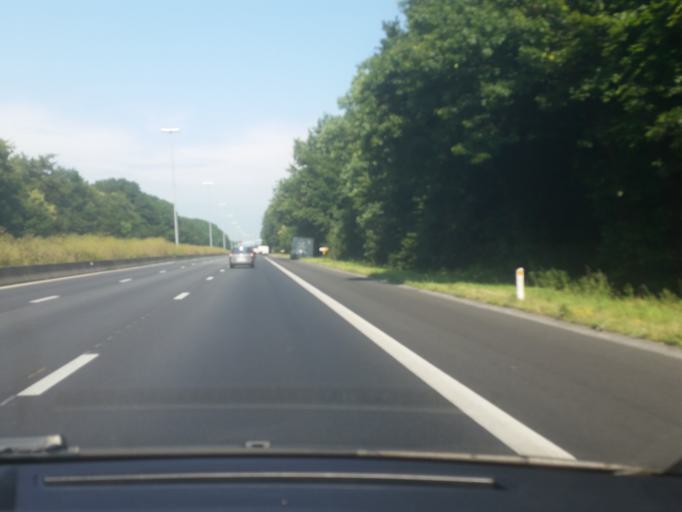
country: BE
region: Flanders
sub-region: Provincie Oost-Vlaanderen
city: Aalter
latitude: 51.0721
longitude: 3.4656
